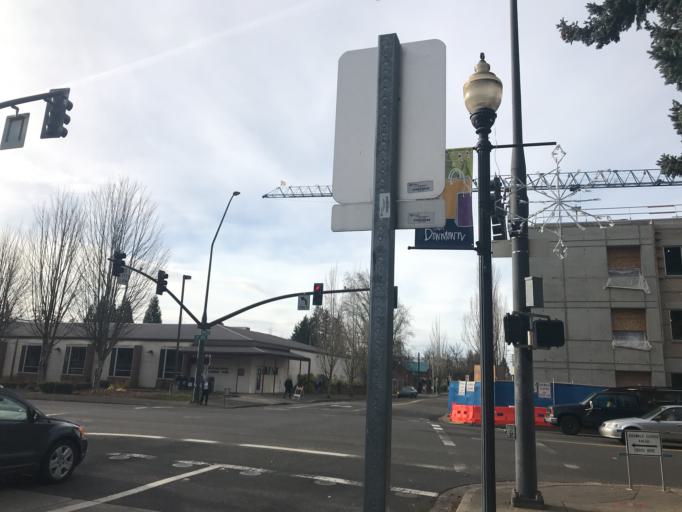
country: US
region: Oregon
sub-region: Washington County
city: Hillsboro
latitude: 45.5228
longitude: -122.9895
